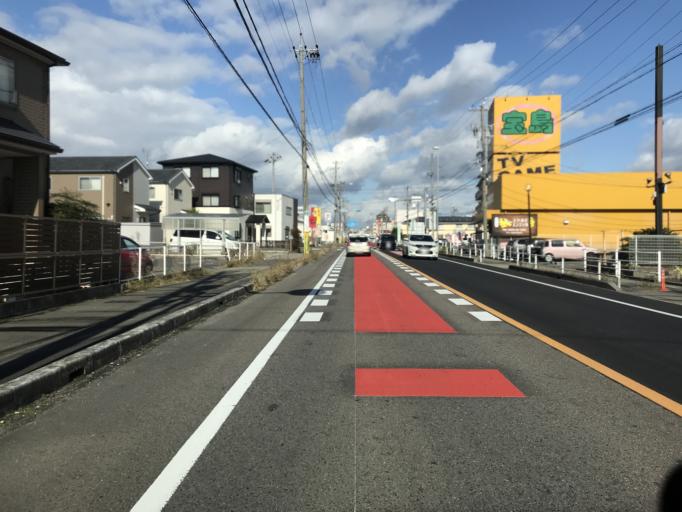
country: JP
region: Aichi
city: Komaki
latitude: 35.2405
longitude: 136.8960
